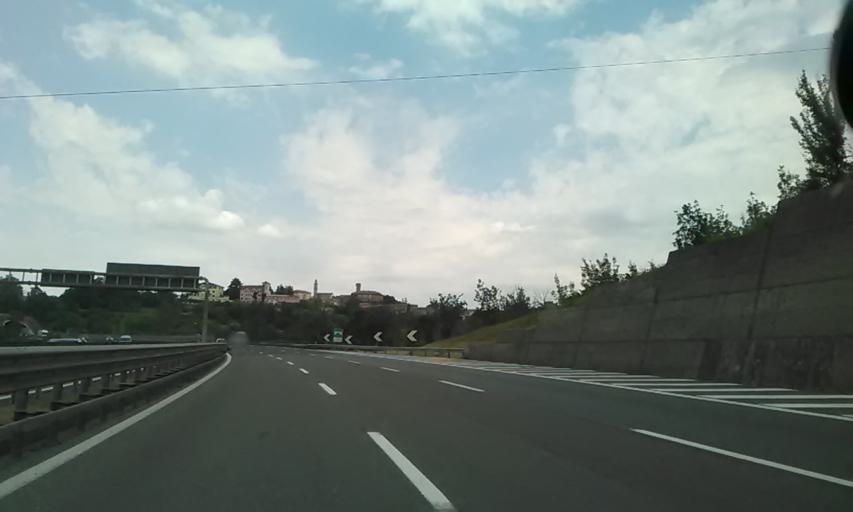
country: IT
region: Piedmont
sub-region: Provincia di Alessandria
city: Belforte Monferrato
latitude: 44.6317
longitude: 8.6620
